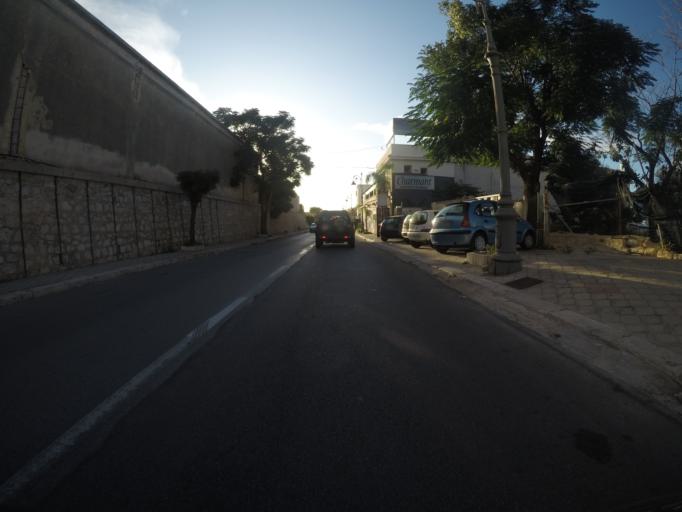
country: IT
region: Sicily
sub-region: Palermo
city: Isola delle Femmine
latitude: 38.1985
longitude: 13.2544
